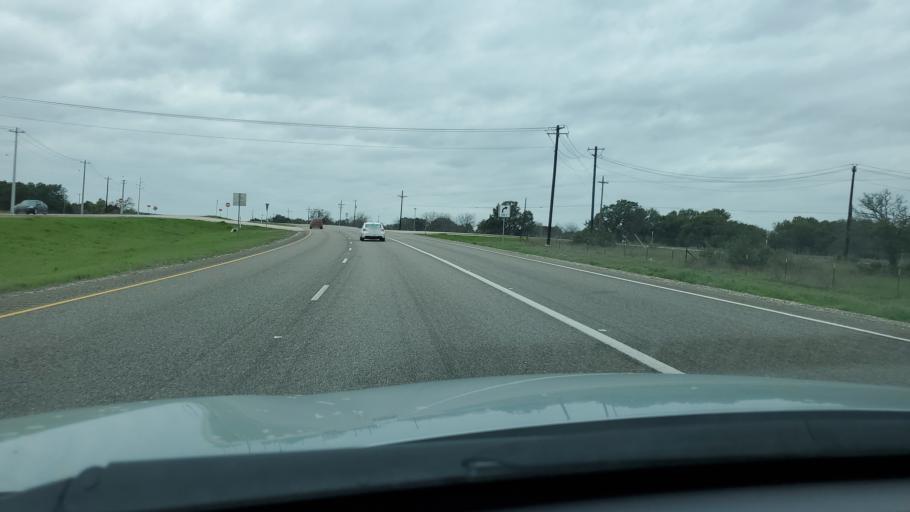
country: US
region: Texas
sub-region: Williamson County
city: Serenada
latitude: 30.7586
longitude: -97.7233
